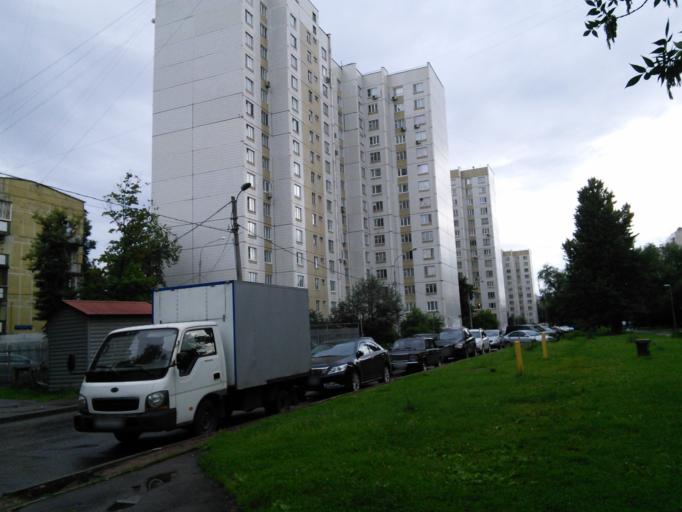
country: RU
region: Moskovskaya
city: Koptevo
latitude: 55.8376
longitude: 37.5316
